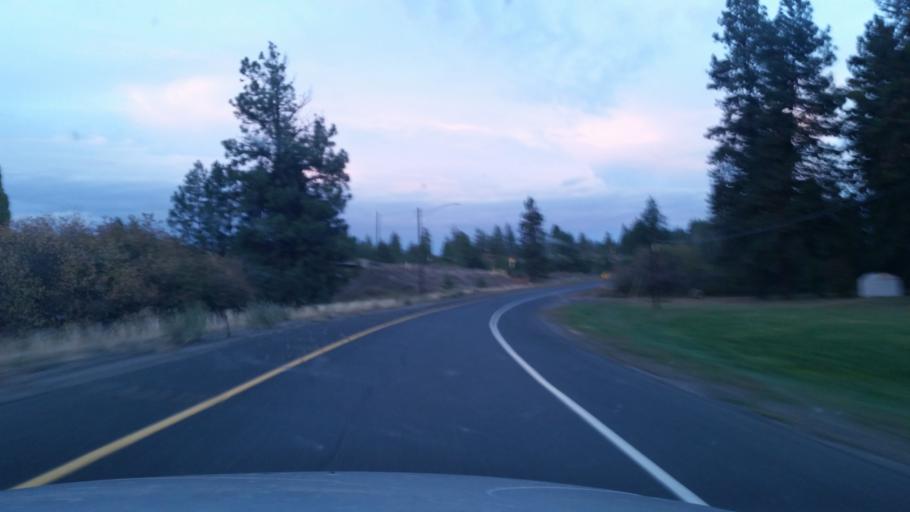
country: US
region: Washington
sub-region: Spokane County
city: Spokane
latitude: 47.6415
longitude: -117.4851
